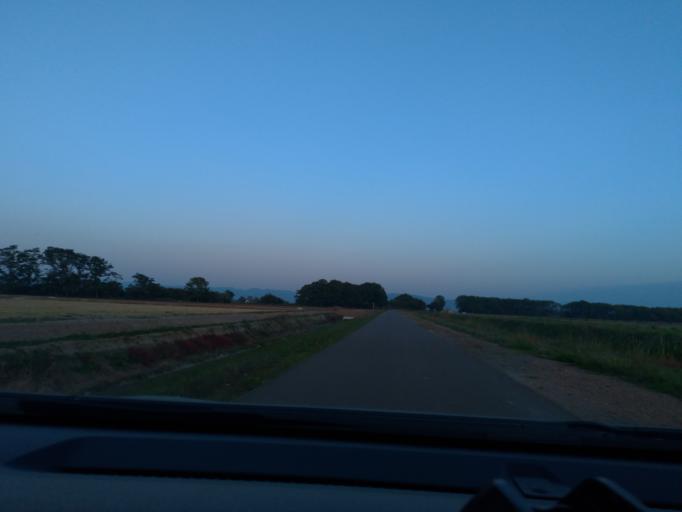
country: JP
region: Hokkaido
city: Iwamizawa
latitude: 43.3305
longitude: 141.7063
